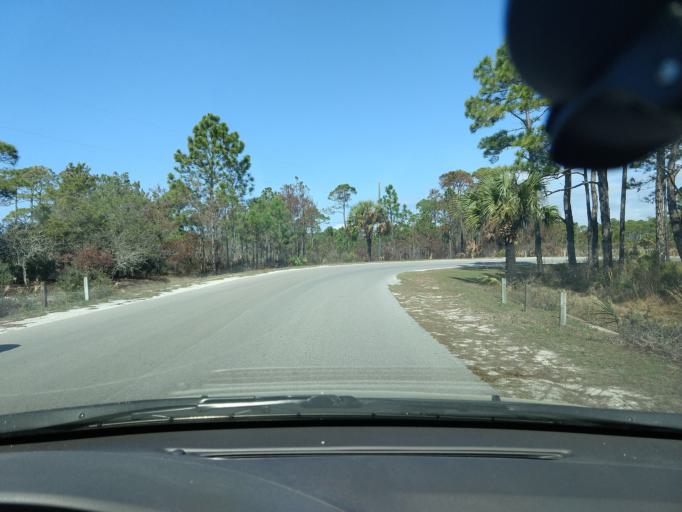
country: US
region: Florida
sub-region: Gulf County
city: Port Saint Joe
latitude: 29.7750
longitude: -85.4037
